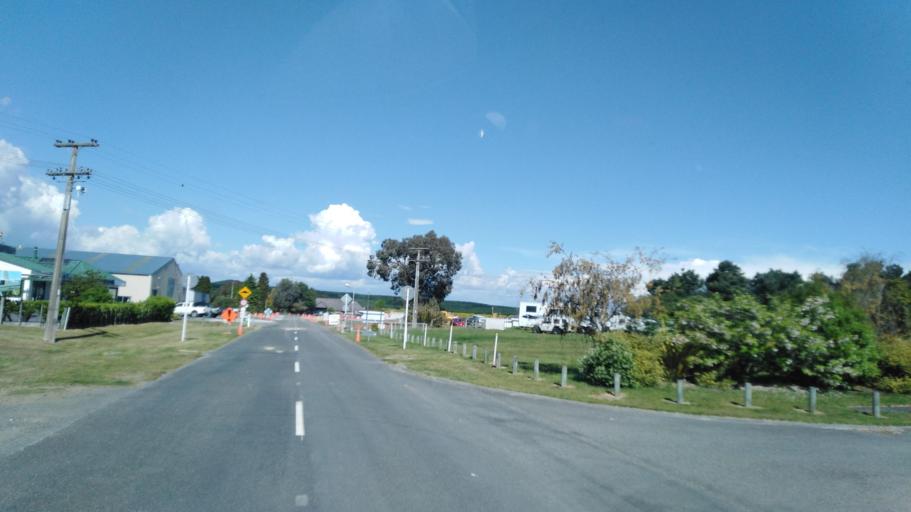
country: NZ
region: Waikato
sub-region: Taupo District
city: Taupo
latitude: -38.7388
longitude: 176.0802
